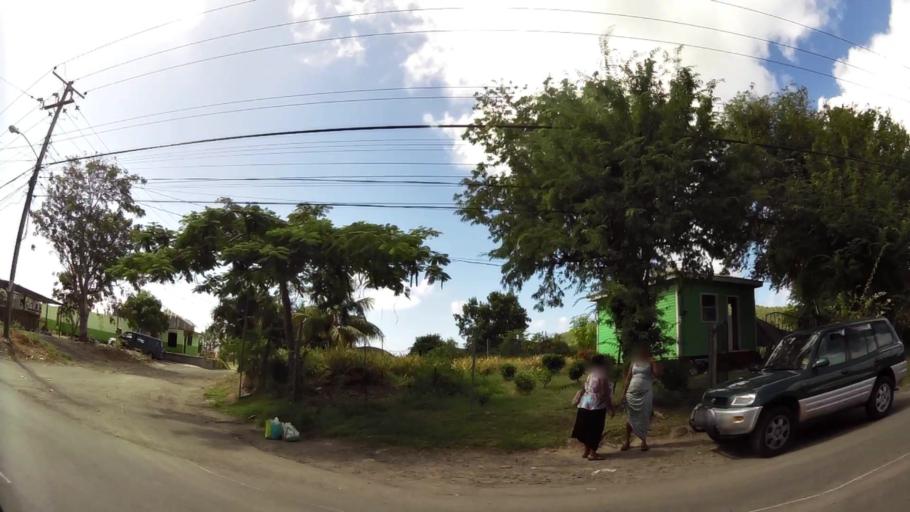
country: LC
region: Laborie Quarter
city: Laborie
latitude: 13.7451
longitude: -60.9824
